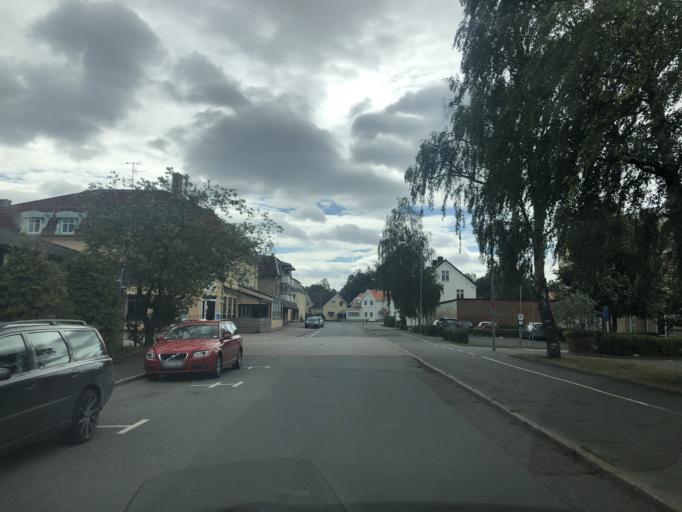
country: SE
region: Joenkoeping
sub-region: Vaggeryds Kommun
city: Vaggeryd
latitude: 57.4979
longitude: 14.1465
